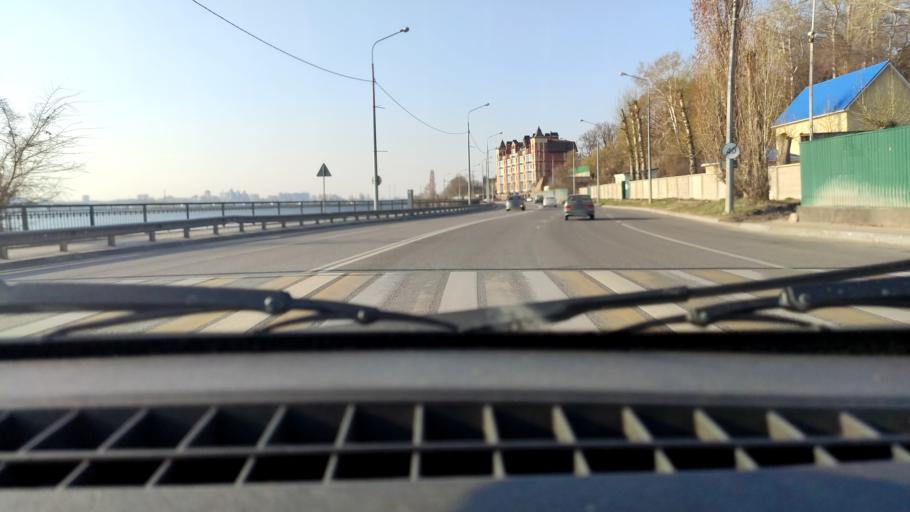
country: RU
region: Voronezj
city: Voronezh
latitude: 51.6830
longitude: 39.2321
